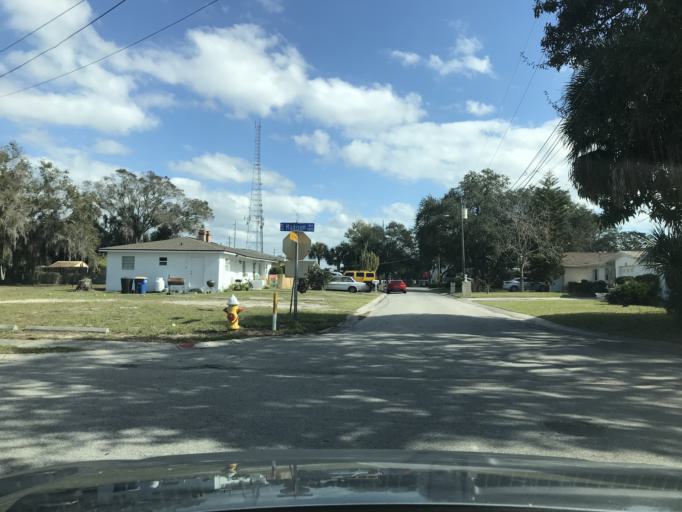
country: US
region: Florida
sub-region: Pinellas County
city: Belleair
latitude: 27.9448
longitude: -82.7896
